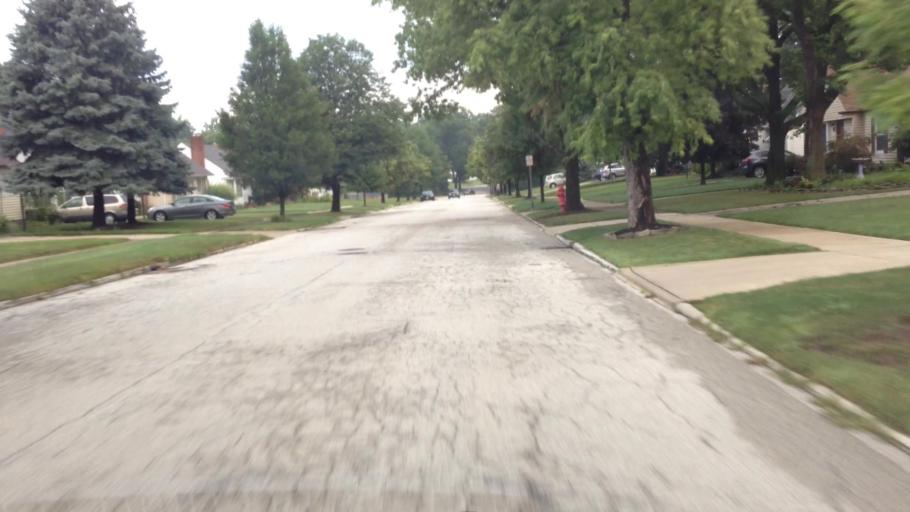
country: US
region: Ohio
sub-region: Cuyahoga County
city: Middleburg Heights
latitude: 41.3621
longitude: -81.8144
